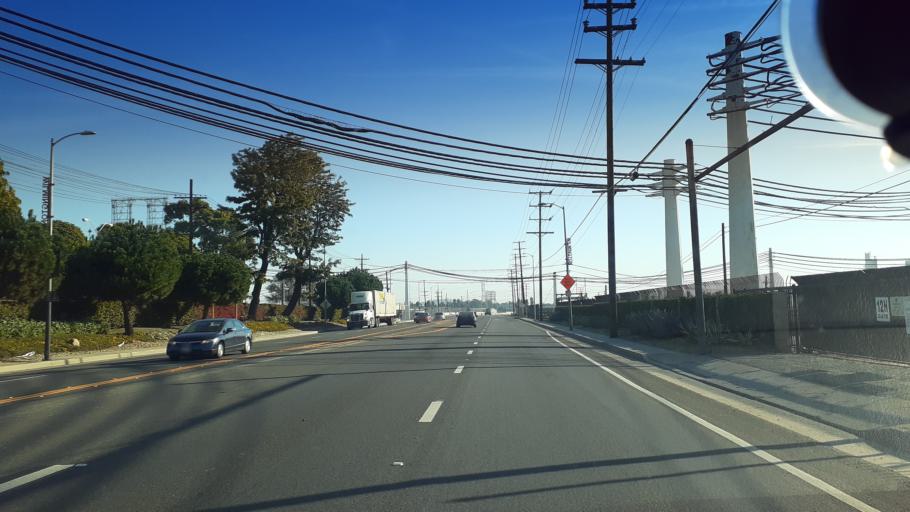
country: US
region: California
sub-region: Los Angeles County
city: Long Beach
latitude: 33.7915
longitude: -118.2351
